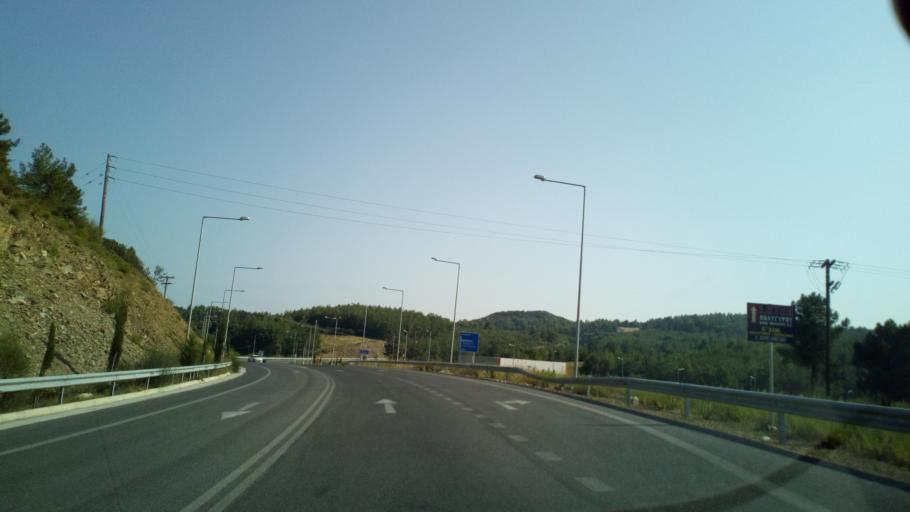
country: GR
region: Central Macedonia
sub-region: Nomos Chalkidikis
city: Polygyros
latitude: 40.3663
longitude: 23.4398
